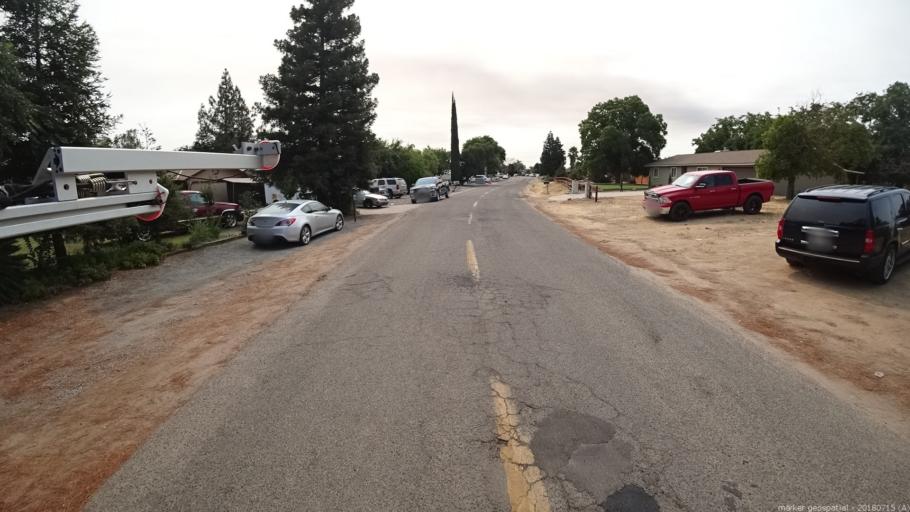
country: US
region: California
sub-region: Madera County
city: Madera Acres
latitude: 37.0011
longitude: -120.0709
